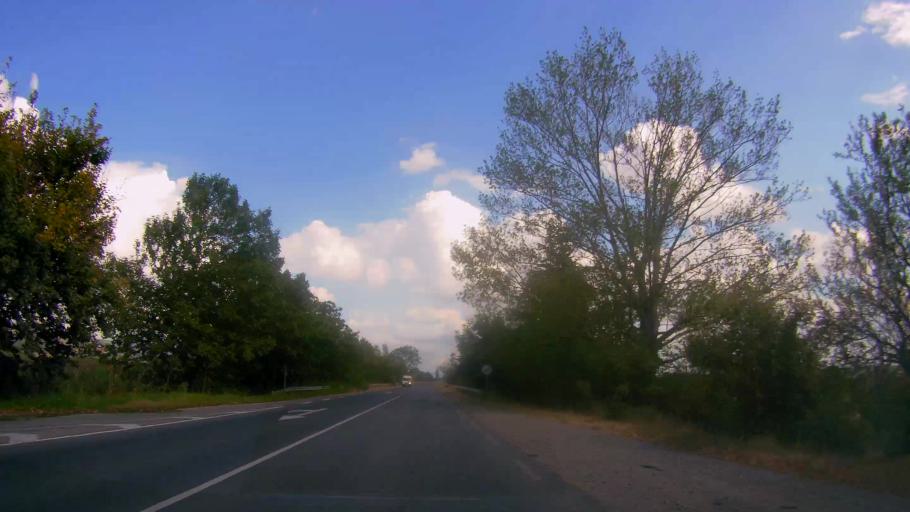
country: BG
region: Sliven
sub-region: Obshtina Sliven
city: Sliven
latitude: 42.6354
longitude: 26.2181
